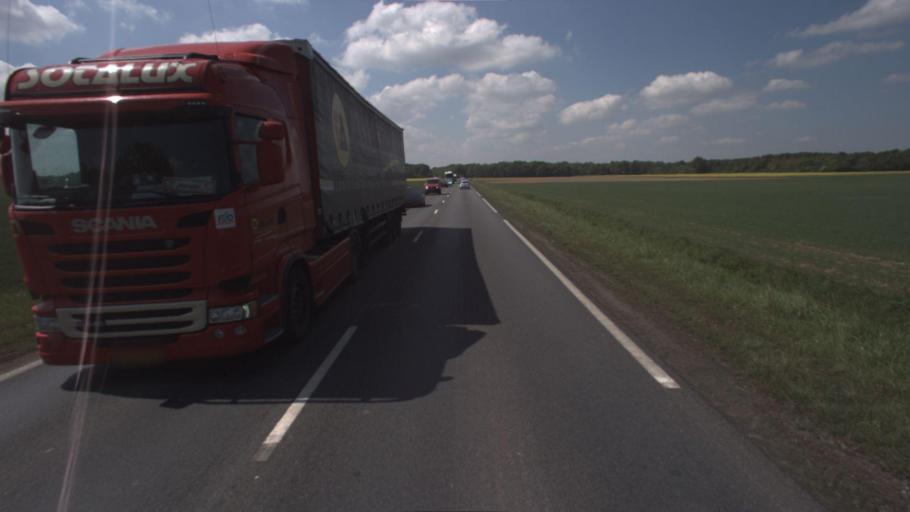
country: FR
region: Ile-de-France
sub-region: Departement de Seine-et-Marne
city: Chaumes-en-Brie
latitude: 48.7036
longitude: 2.8317
